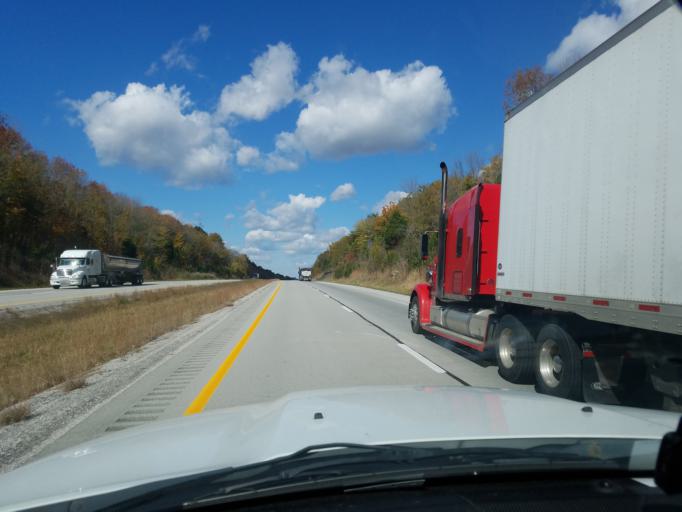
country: US
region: Kentucky
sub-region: Butler County
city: Morgantown
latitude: 37.2545
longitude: -86.7417
